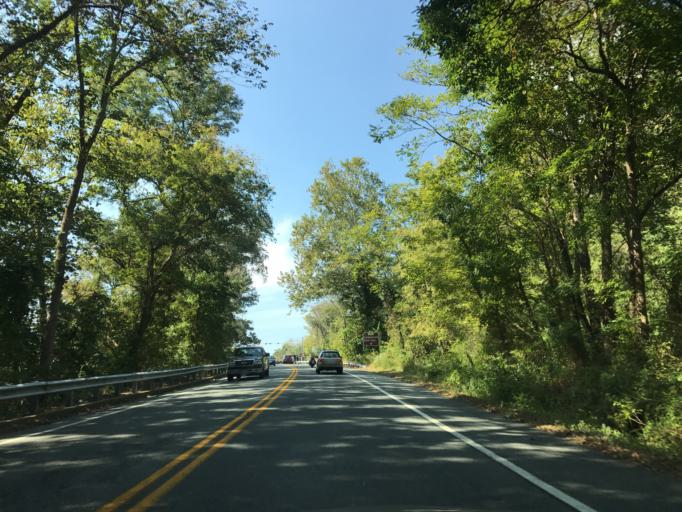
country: US
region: Maryland
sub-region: Cecil County
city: Rising Sun
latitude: 39.6669
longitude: -76.1683
